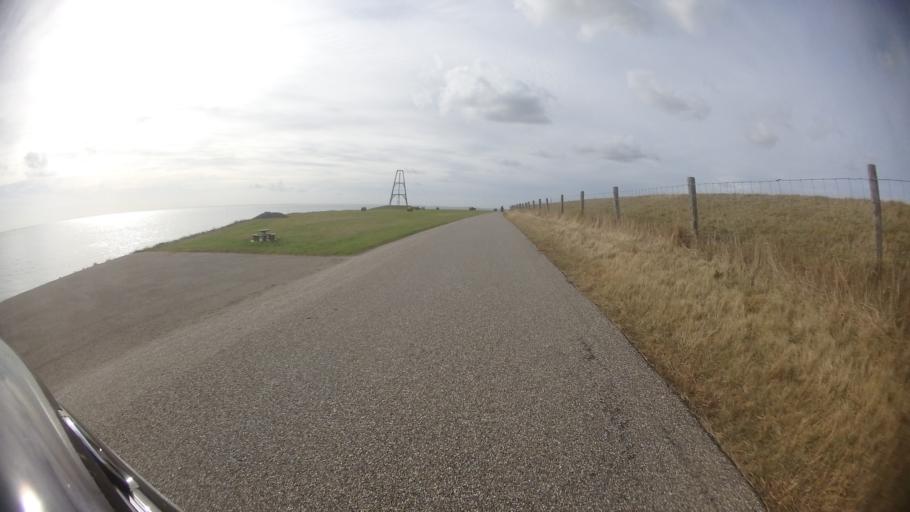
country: NL
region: North Holland
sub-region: Gemeente Texel
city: Den Burg
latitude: 53.0799
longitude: 4.8972
